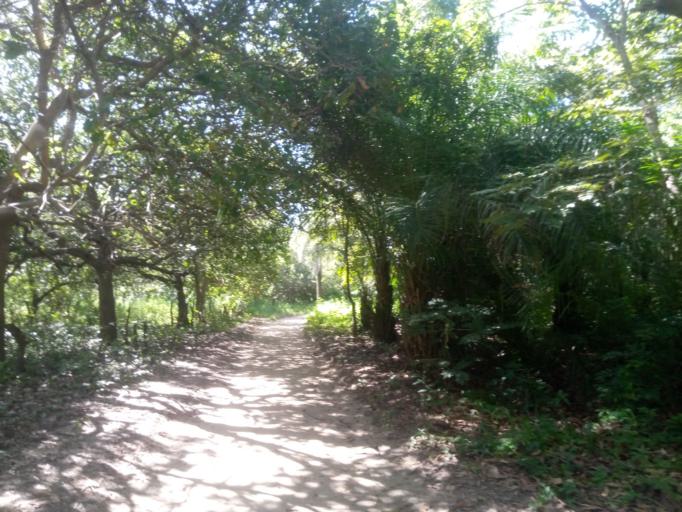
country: GM
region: Western
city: Gunjur
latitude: 13.0406
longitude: -16.7291
